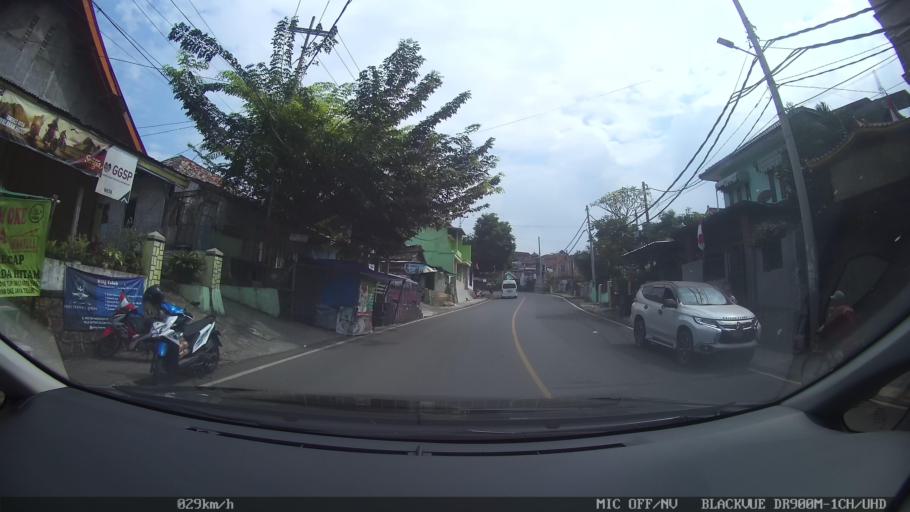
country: ID
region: Lampung
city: Bandarlampung
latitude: -5.4450
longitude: 105.2611
